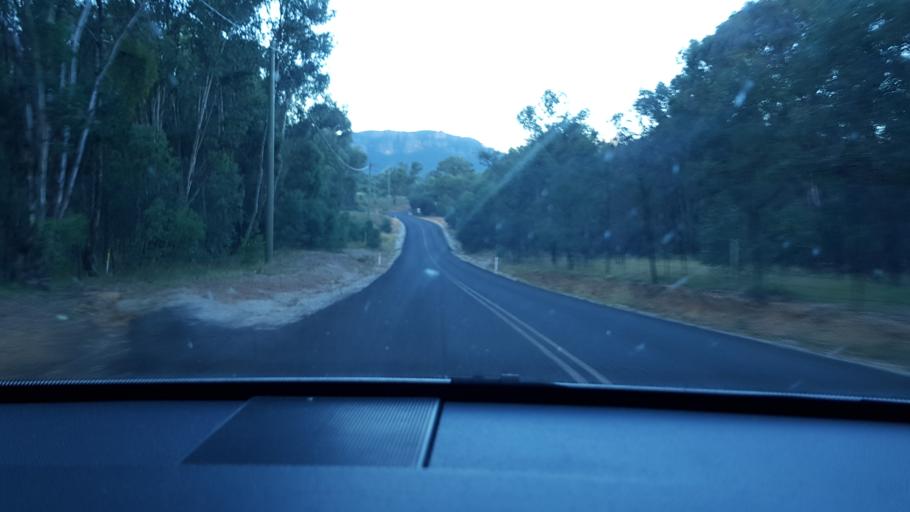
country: AU
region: New South Wales
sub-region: Lithgow
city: Portland
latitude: -33.2554
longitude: 150.1393
